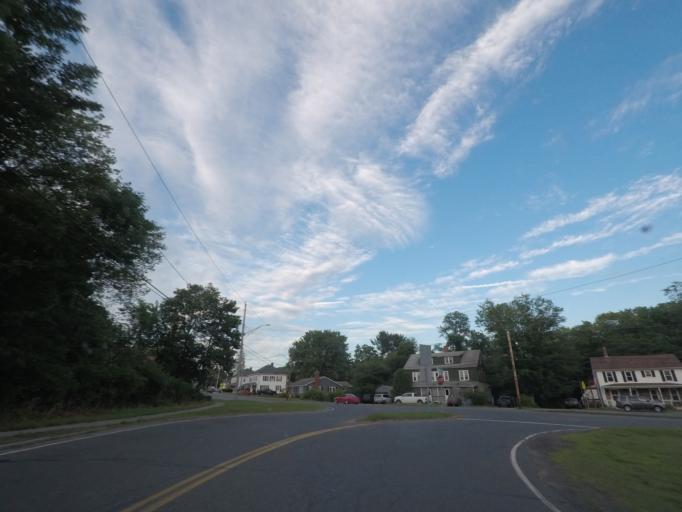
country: US
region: Massachusetts
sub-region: Hampshire County
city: Ware
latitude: 42.2120
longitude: -72.2424
